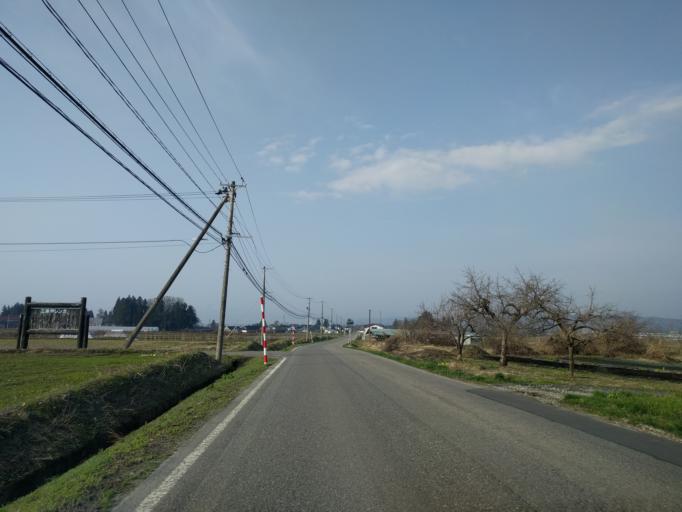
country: JP
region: Fukushima
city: Kitakata
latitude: 37.6823
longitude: 139.9008
